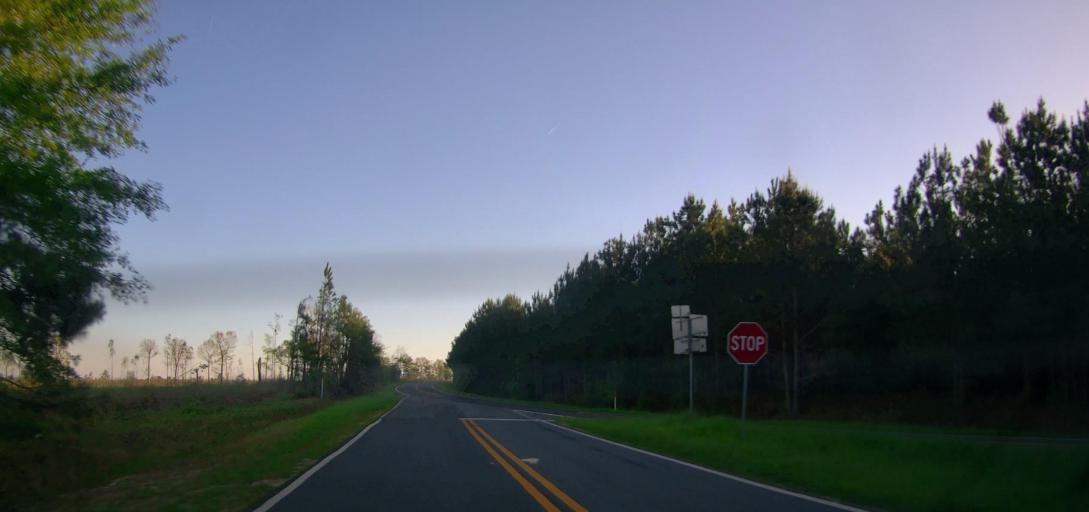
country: US
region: Georgia
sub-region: Marion County
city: Buena Vista
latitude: 32.4324
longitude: -84.4281
